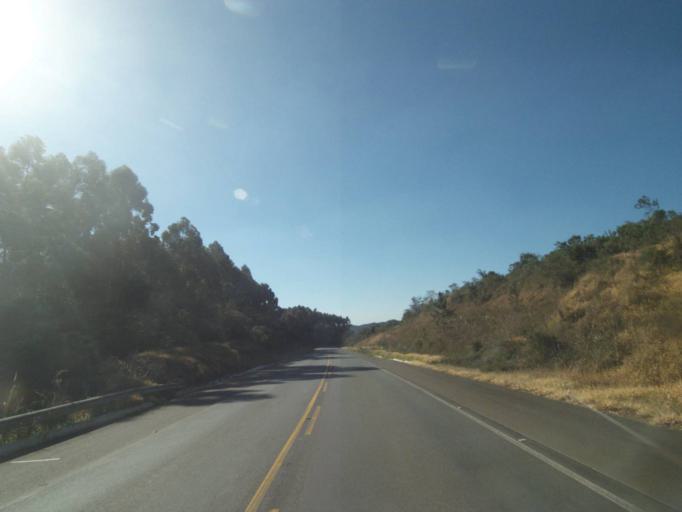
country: BR
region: Parana
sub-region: Tibagi
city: Tibagi
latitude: -24.7528
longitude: -50.4660
